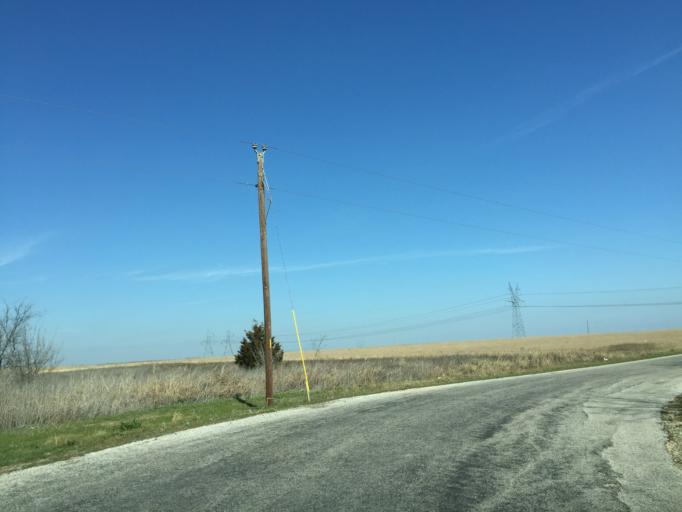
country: US
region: Texas
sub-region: Williamson County
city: Granger
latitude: 30.7588
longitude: -97.5283
